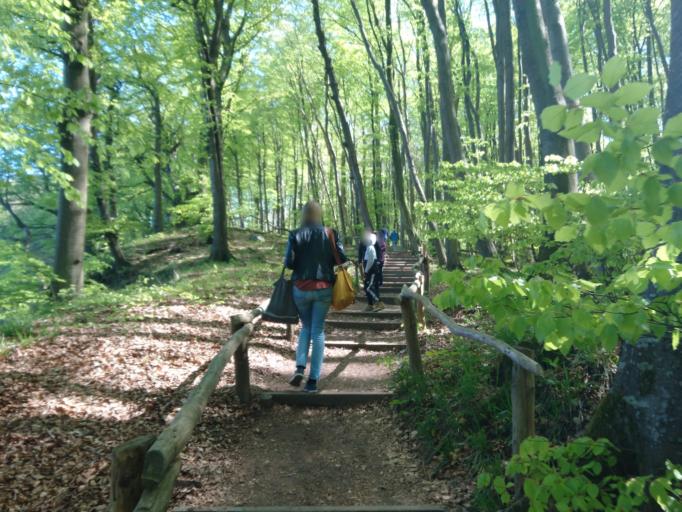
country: DE
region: Mecklenburg-Vorpommern
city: Sassnitz
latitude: 54.5715
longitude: 13.6617
